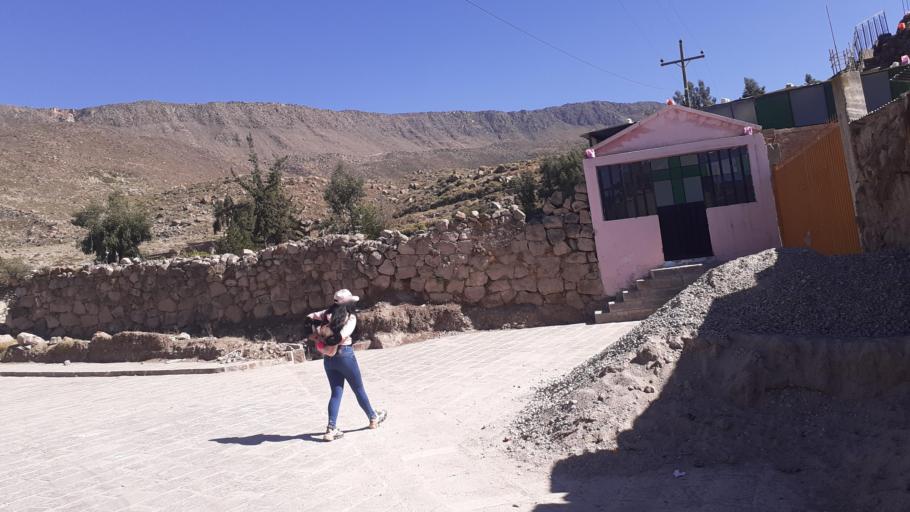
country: PE
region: Arequipa
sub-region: Provincia de Condesuyos
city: Chuquibamba
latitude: -15.8375
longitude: -72.6563
